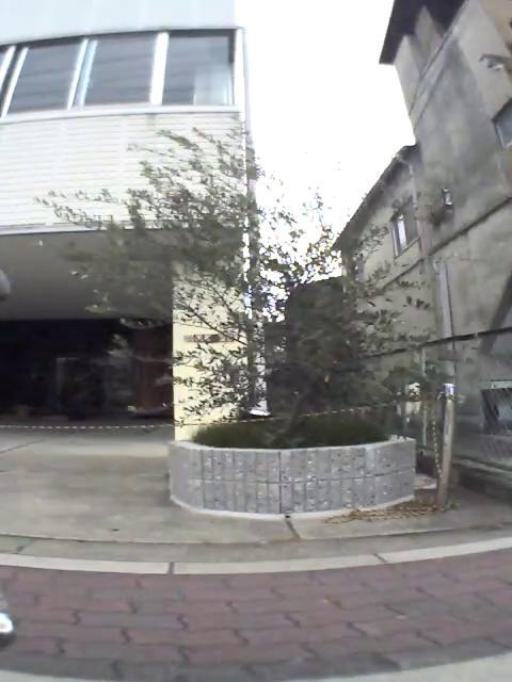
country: JP
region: Osaka
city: Neyagawa
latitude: 34.7832
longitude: 135.6321
